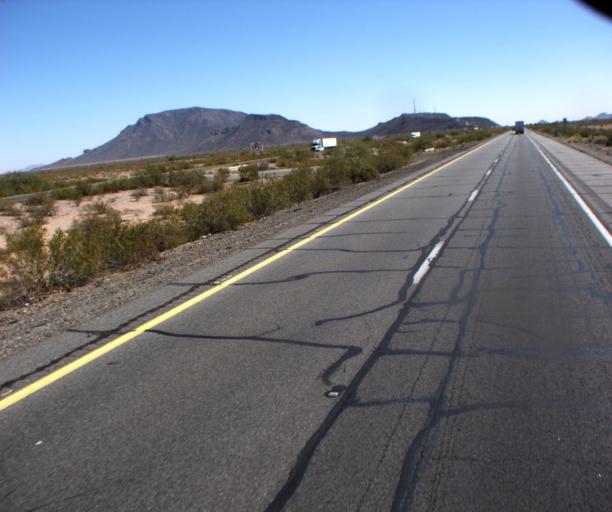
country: US
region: Arizona
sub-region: La Paz County
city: Salome
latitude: 33.5348
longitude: -113.1442
